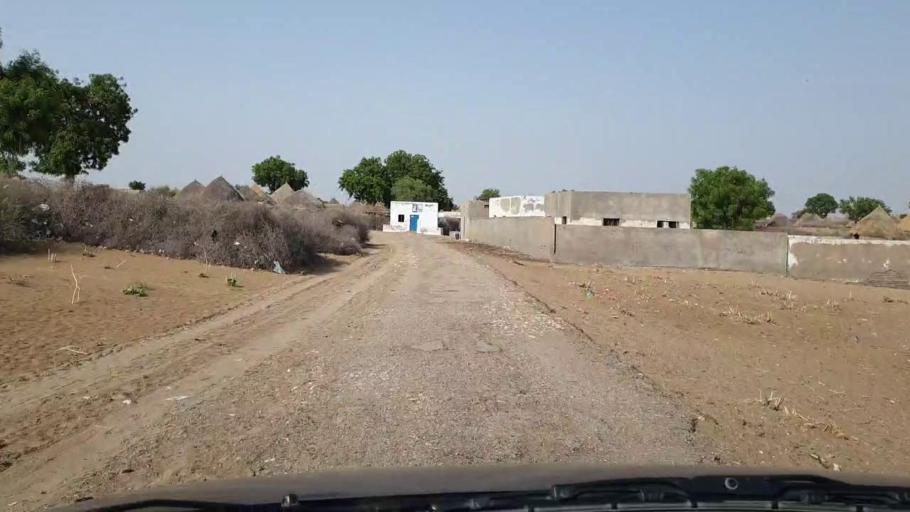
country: PK
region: Sindh
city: Chor
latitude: 25.4565
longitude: 70.5347
